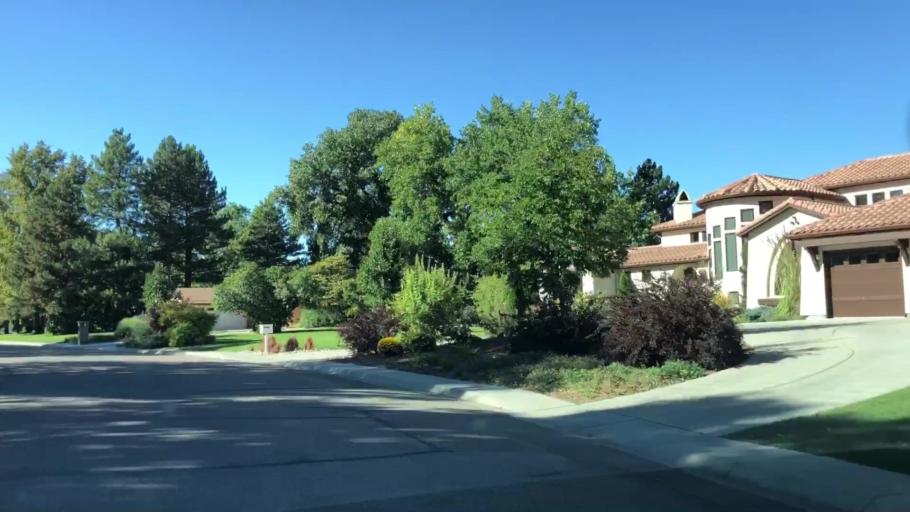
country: US
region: Colorado
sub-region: Larimer County
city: Fort Collins
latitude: 40.5555
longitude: -105.0538
